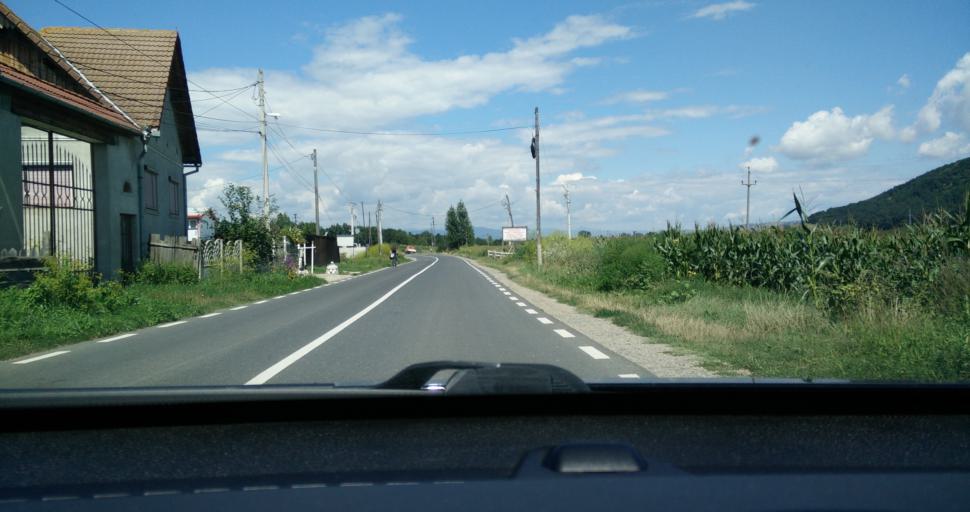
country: RO
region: Alba
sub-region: Comuna Sasciori
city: Sebesel
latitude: 45.8922
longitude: 23.5614
